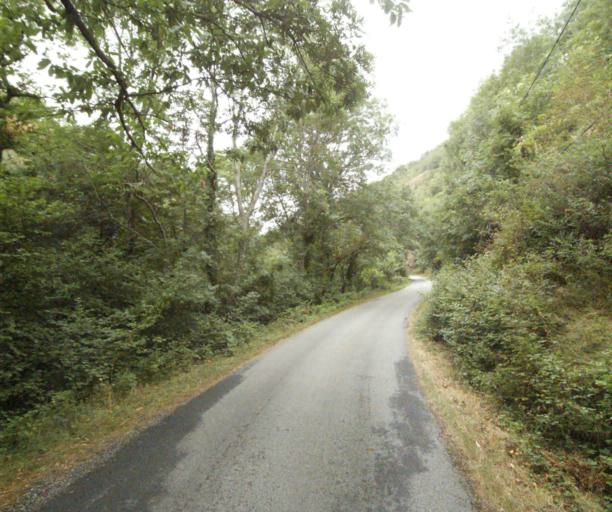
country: FR
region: Midi-Pyrenees
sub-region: Departement du Tarn
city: Soreze
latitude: 43.4314
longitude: 2.0752
